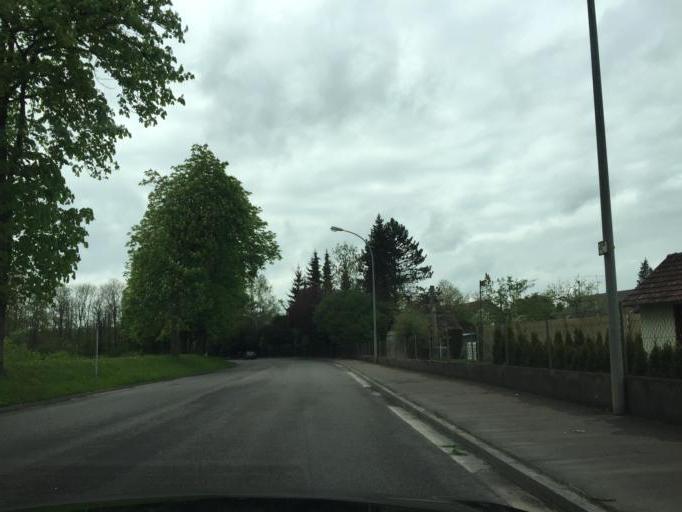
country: DE
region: Bavaria
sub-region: Swabia
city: Dillingen an der Donau
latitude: 48.5718
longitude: 10.4925
